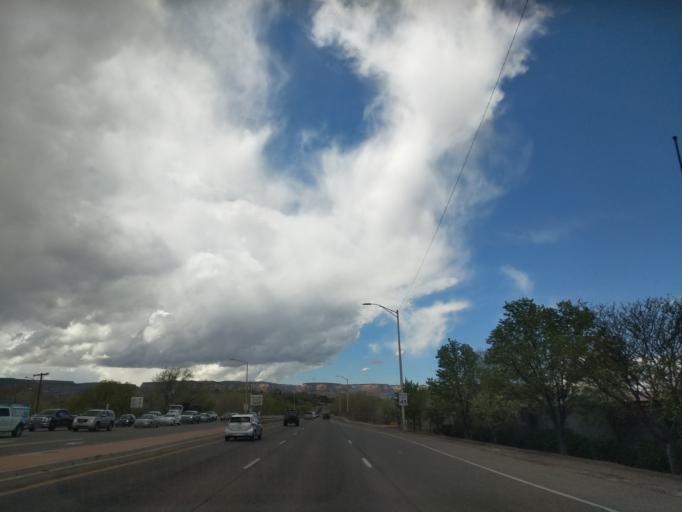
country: US
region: Colorado
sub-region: Mesa County
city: Grand Junction
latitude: 39.0683
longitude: -108.5794
